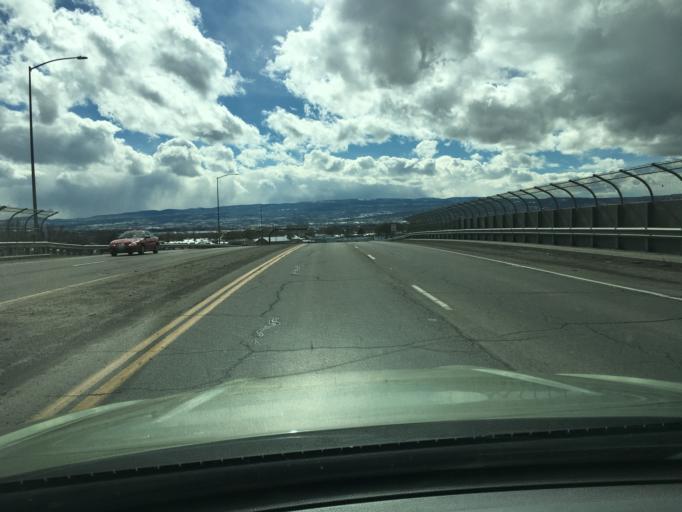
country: US
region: Colorado
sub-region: Mesa County
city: Clifton
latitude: 39.0862
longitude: -108.4573
